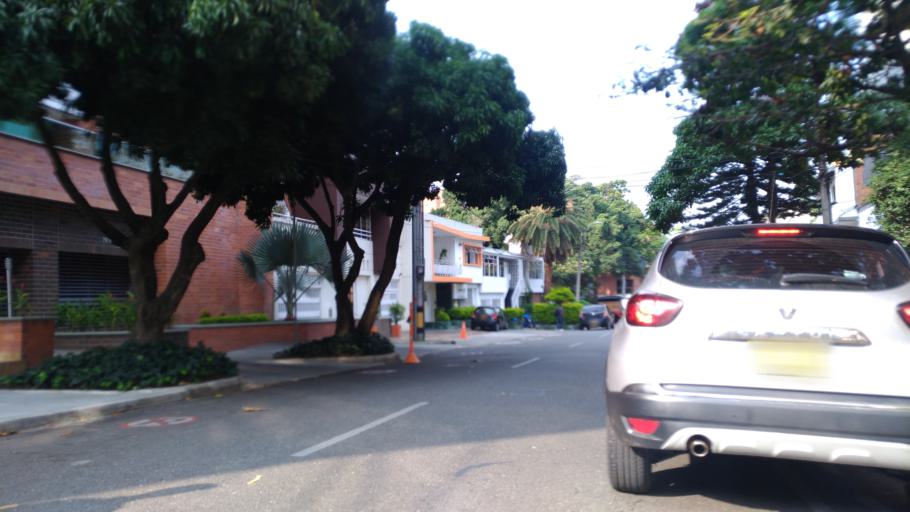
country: CO
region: Antioquia
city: Medellin
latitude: 6.2439
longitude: -75.5920
